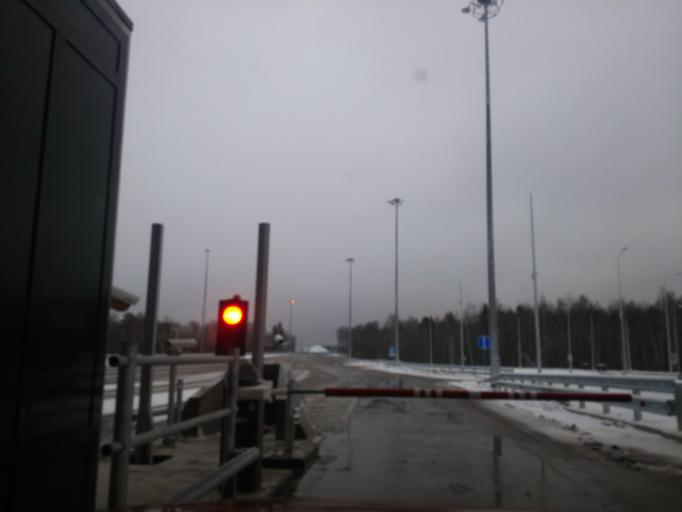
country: RU
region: Tverskaya
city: Likhoslavl'
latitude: 56.9551
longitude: 35.5063
